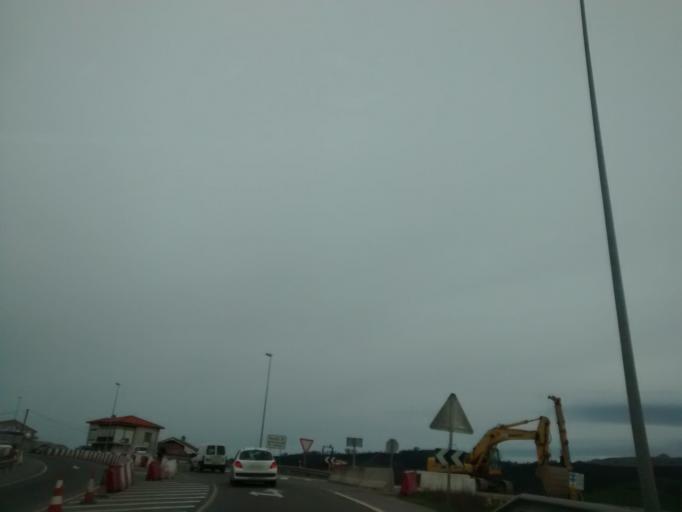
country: ES
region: Cantabria
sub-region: Provincia de Cantabria
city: Santa Maria de Cayon
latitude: 43.3313
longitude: -3.8413
